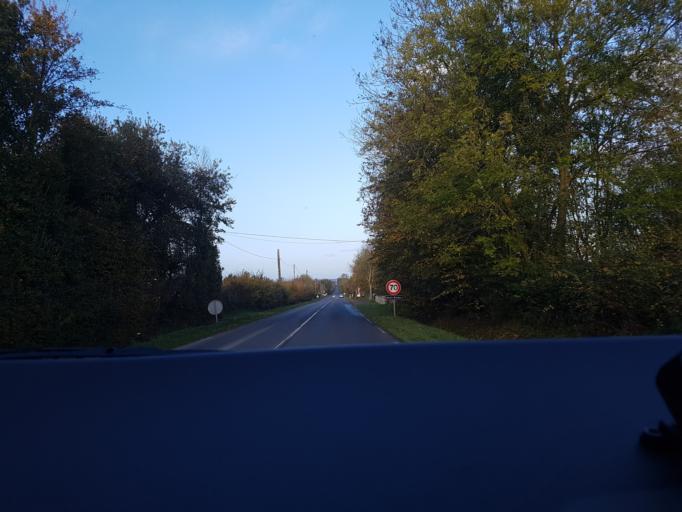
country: FR
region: Lower Normandy
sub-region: Departement du Calvados
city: Troarn
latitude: 49.1984
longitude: -0.1323
